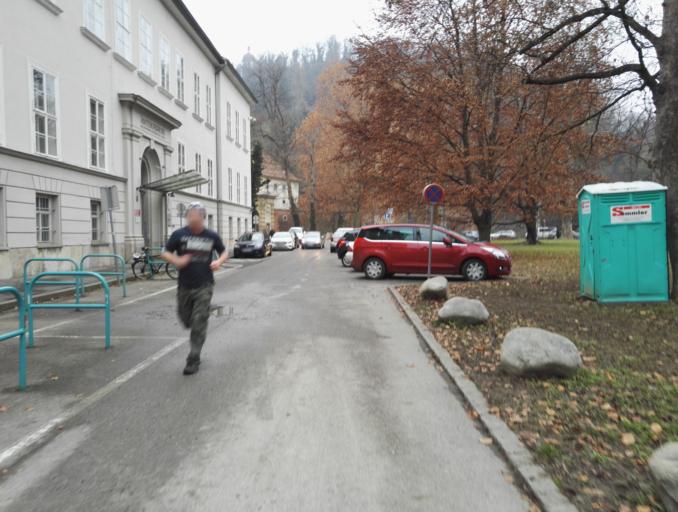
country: AT
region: Styria
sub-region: Graz Stadt
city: Graz
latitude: 47.0761
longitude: 15.4422
